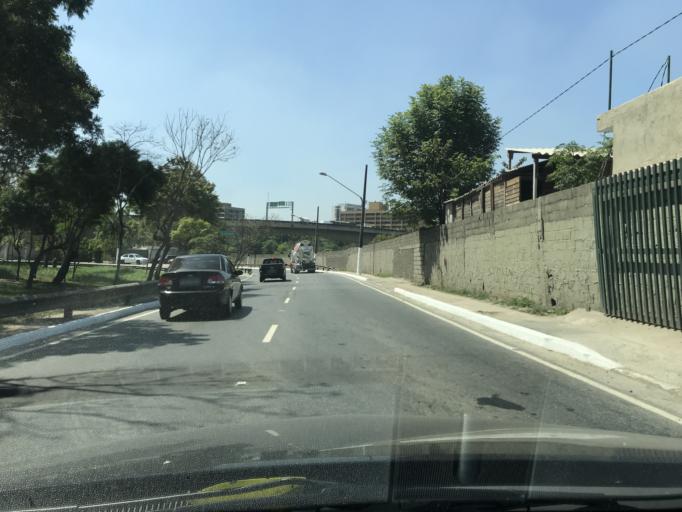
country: BR
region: Sao Paulo
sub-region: Taboao Da Serra
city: Taboao da Serra
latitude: -23.6542
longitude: -46.7241
